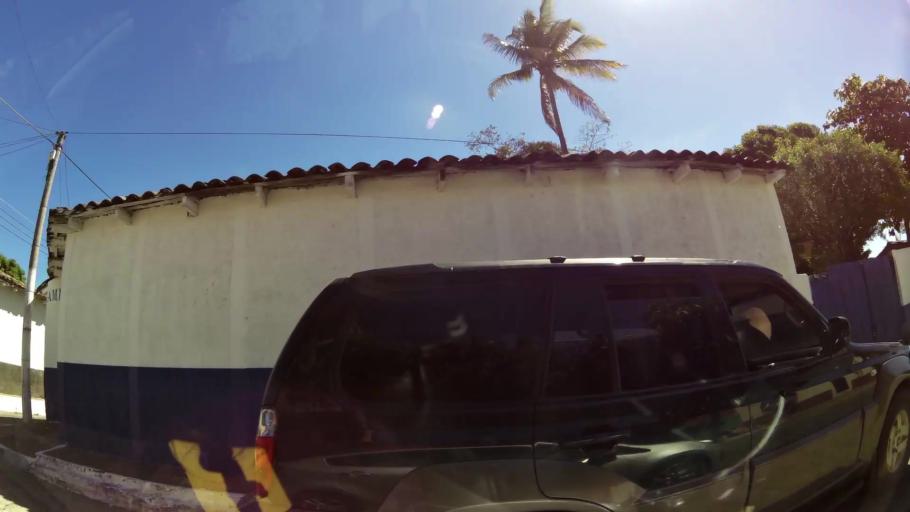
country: SV
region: La Libertad
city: San Juan Opico
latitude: 13.8753
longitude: -89.3578
